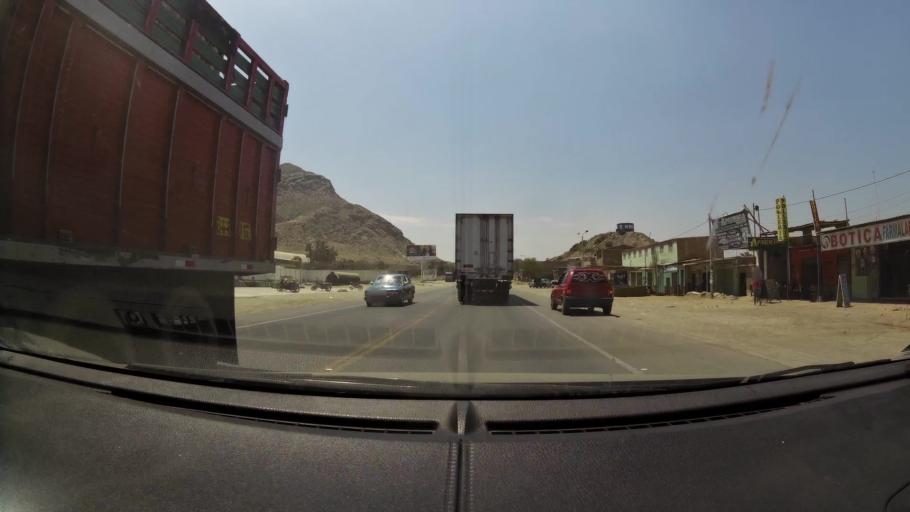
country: PE
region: La Libertad
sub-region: Provincia de Pacasmayo
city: Guadalupe
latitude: -7.3033
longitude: -79.4782
